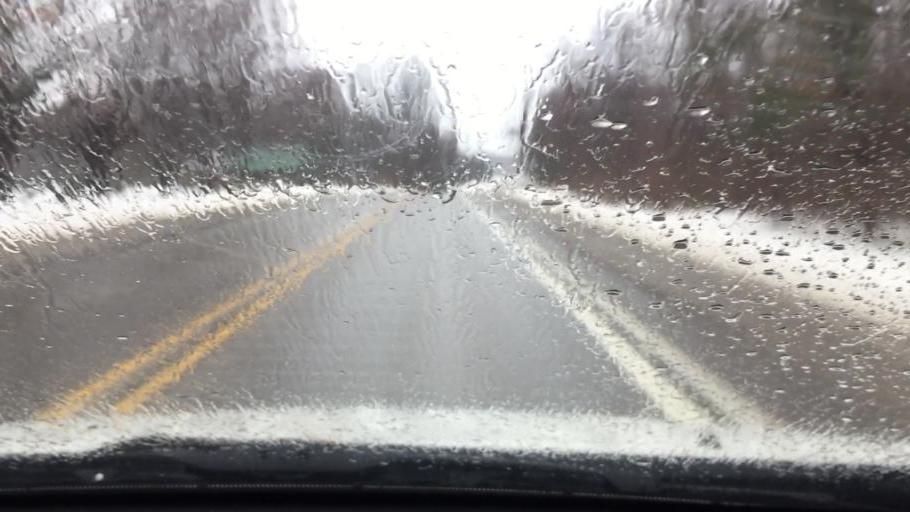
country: US
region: Michigan
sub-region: Charlevoix County
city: East Jordan
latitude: 45.1778
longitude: -85.1638
